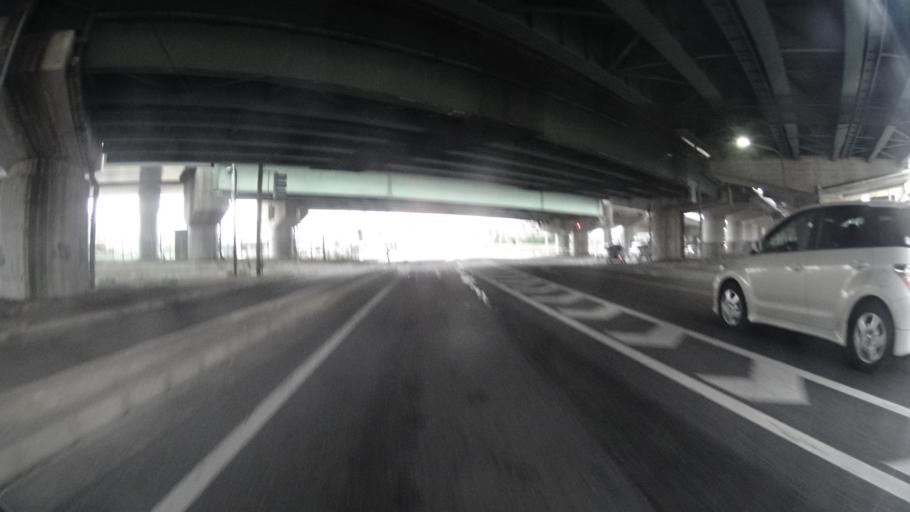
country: JP
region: Fukuoka
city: Onojo
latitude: 33.5243
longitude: 130.4957
